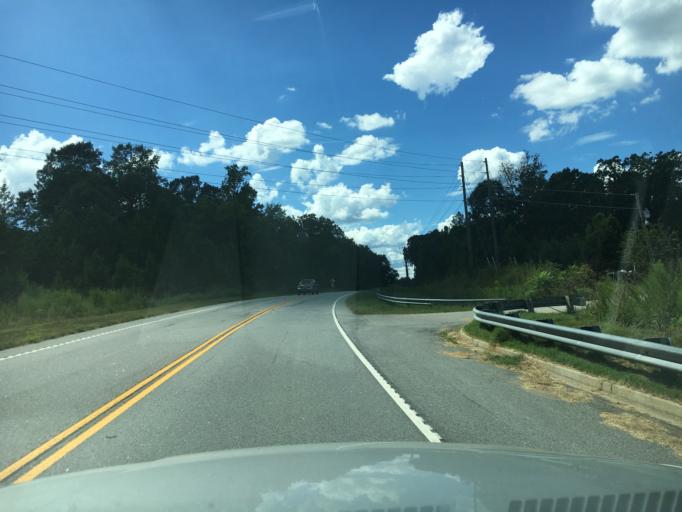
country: US
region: South Carolina
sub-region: Laurens County
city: Laurens
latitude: 34.5218
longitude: -82.1431
